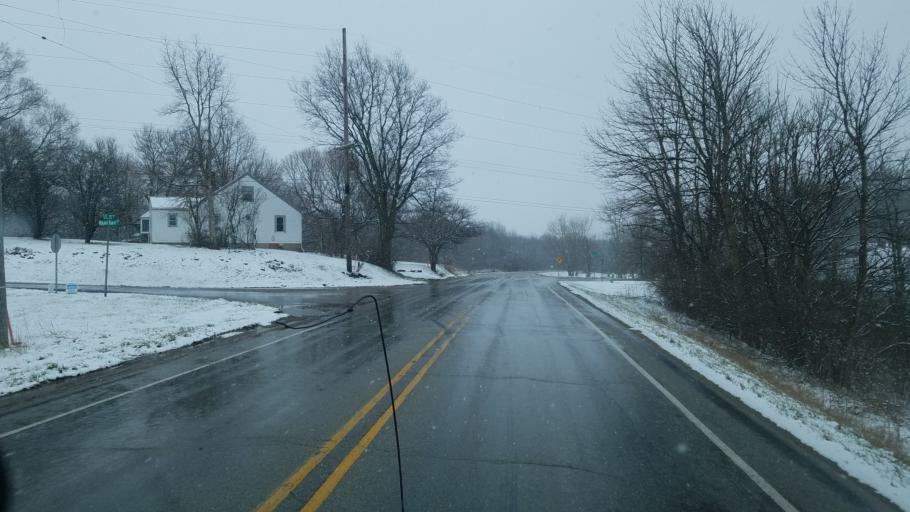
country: US
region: Indiana
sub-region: Wayne County
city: Centerville
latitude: 39.9236
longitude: -84.9591
